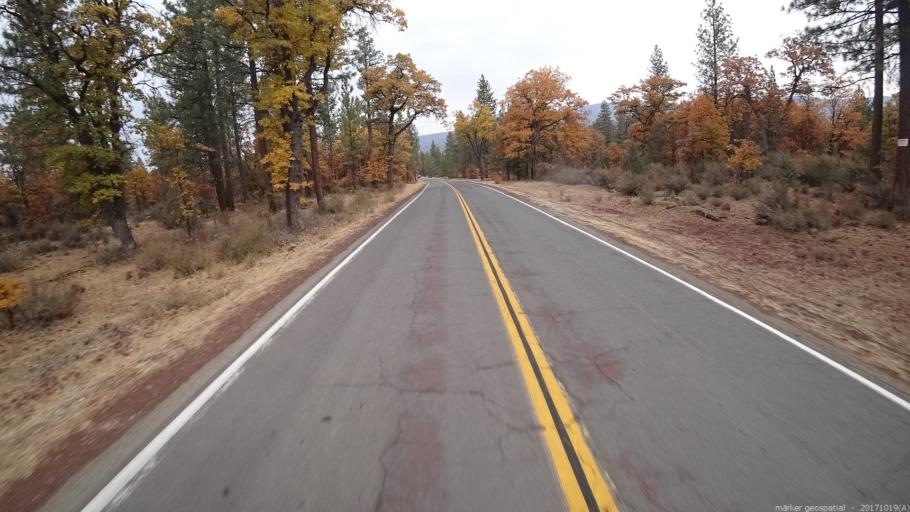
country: US
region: California
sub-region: Shasta County
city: Burney
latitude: 41.1142
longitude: -121.3319
